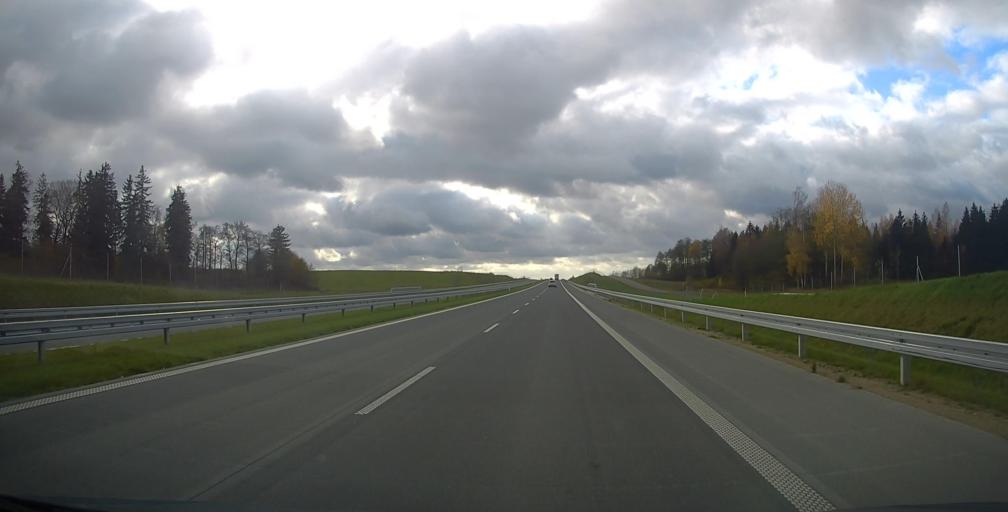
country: PL
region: Podlasie
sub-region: Powiat suwalski
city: Raczki
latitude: 53.8938
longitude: 22.6835
